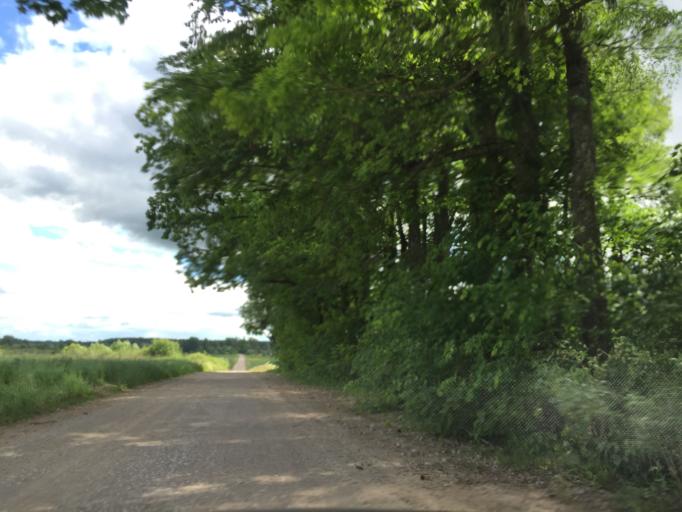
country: LV
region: Vecumnieki
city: Vecumnieki
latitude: 56.4797
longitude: 24.4161
